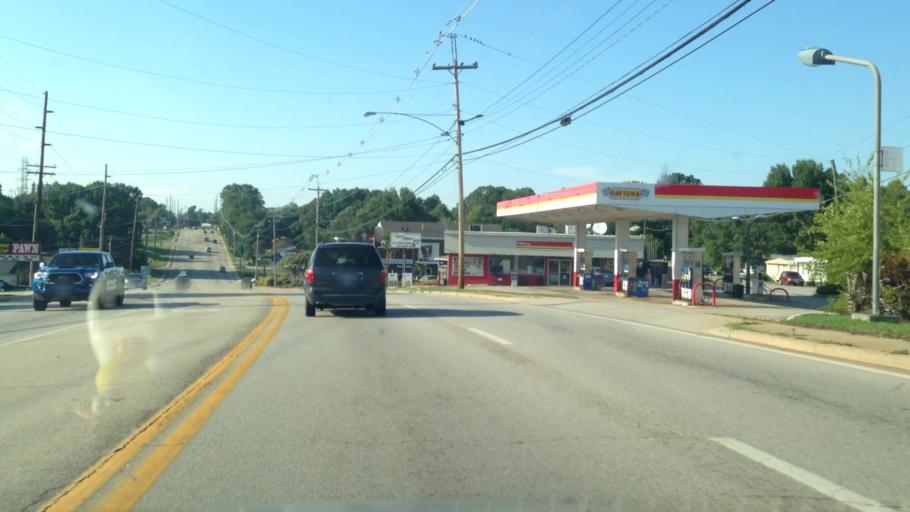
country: US
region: Virginia
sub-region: City of Danville
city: Danville
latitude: 36.6117
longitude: -79.4056
